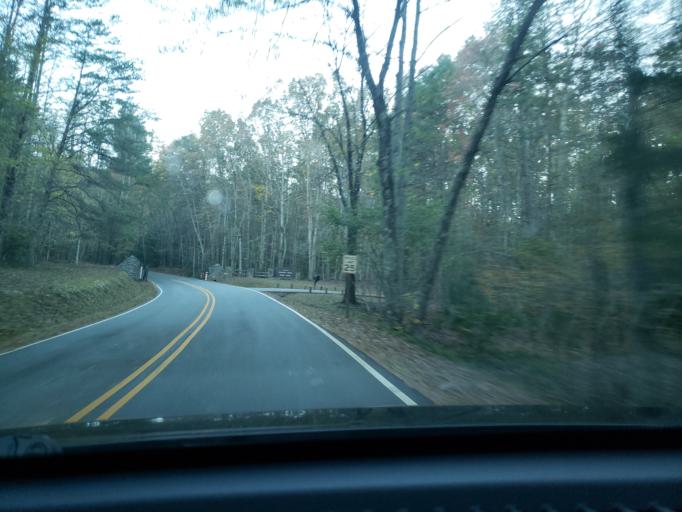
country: US
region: North Carolina
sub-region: Stokes County
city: Danbury
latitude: 36.4120
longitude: -80.2538
